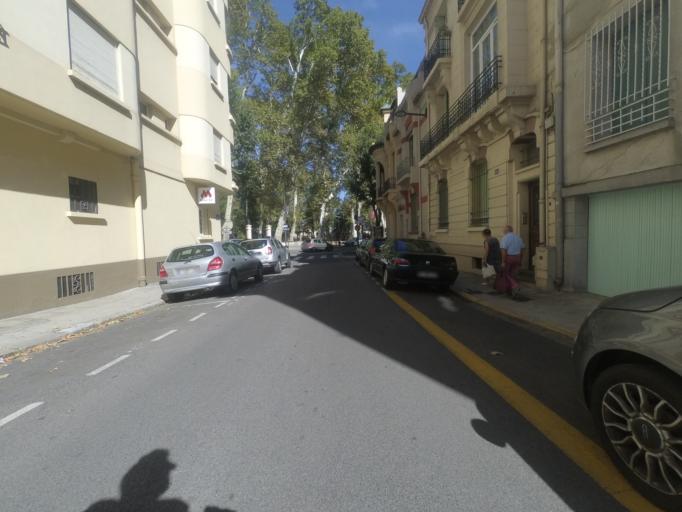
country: FR
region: Languedoc-Roussillon
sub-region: Departement des Pyrenees-Orientales
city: Perpignan
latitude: 42.7017
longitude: 2.8986
